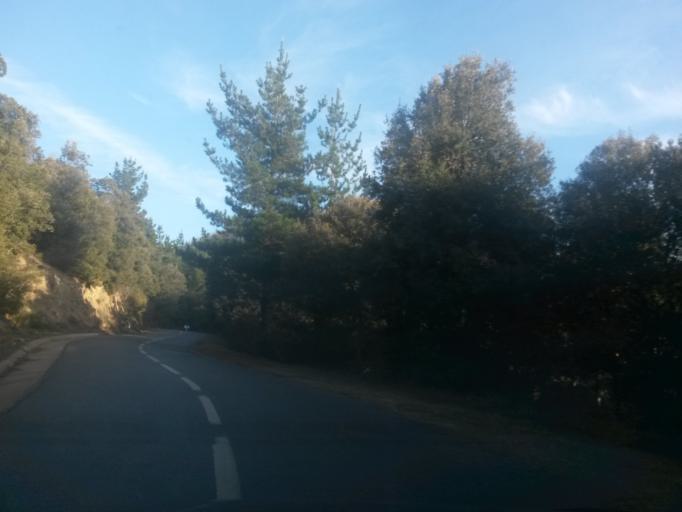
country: ES
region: Catalonia
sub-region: Provincia de Girona
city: Sant Hilari Sacalm
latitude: 41.8652
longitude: 2.5294
